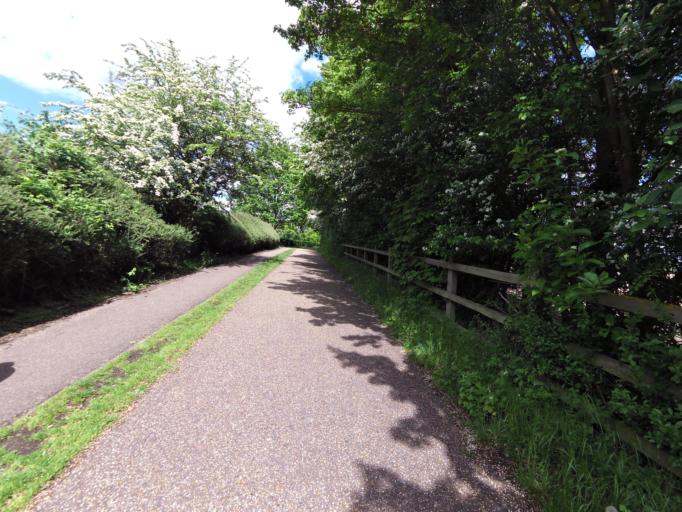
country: GB
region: England
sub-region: Suffolk
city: Bury St Edmunds
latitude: 52.2436
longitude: 0.7235
